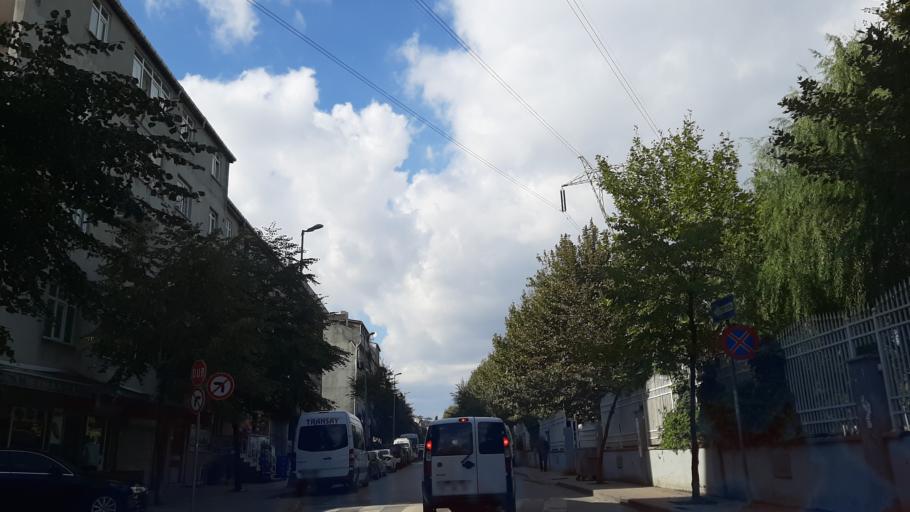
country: TR
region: Istanbul
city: Esenyurt
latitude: 41.0334
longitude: 28.6603
